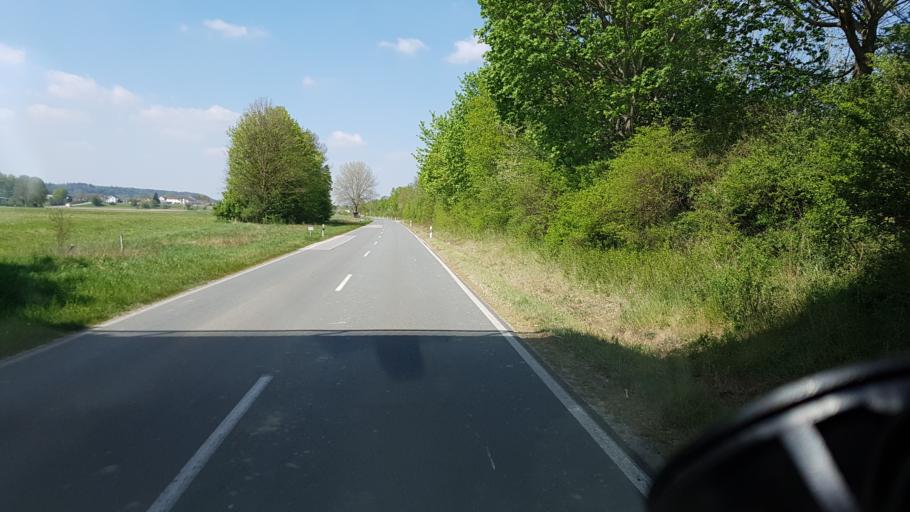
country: DE
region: Bavaria
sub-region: Upper Bavaria
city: Perach
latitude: 48.2507
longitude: 12.7719
